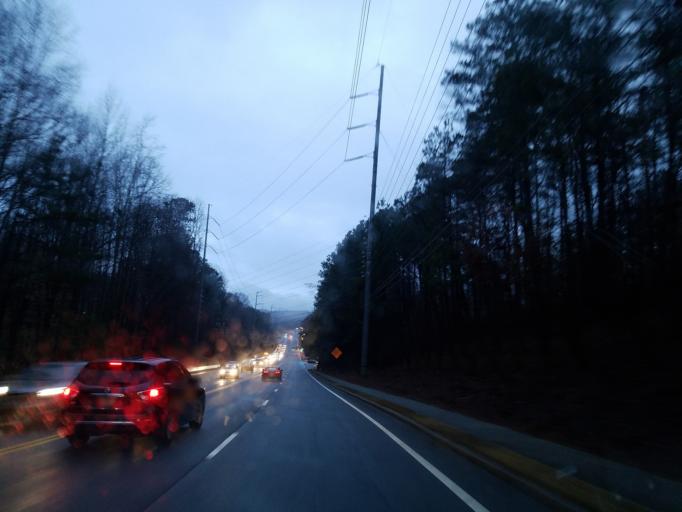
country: US
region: Georgia
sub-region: Fulton County
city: Roswell
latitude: 34.0112
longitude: -84.3023
